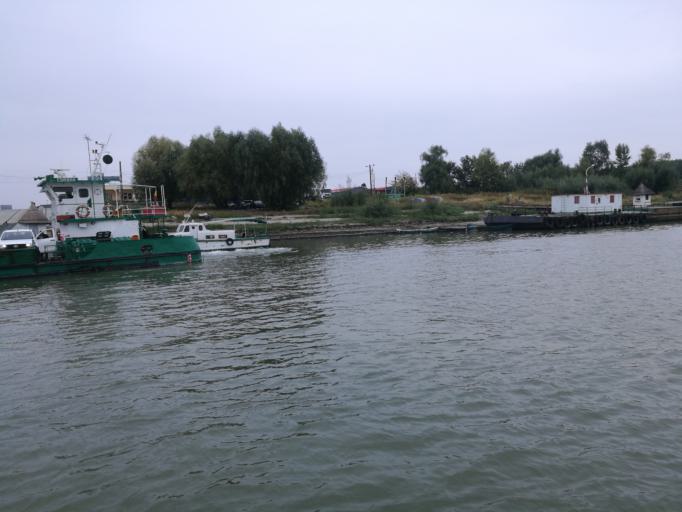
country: RO
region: Braila
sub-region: Municipiul Braila
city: Braila
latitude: 45.2892
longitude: 27.9927
